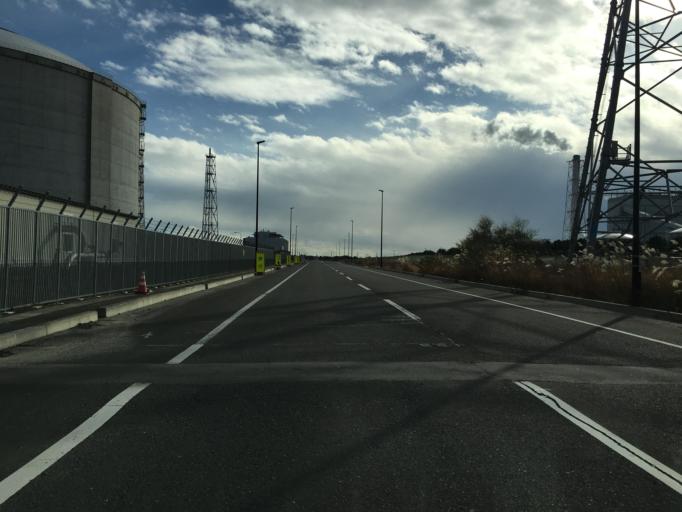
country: JP
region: Miyagi
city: Marumori
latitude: 37.8514
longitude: 140.9480
